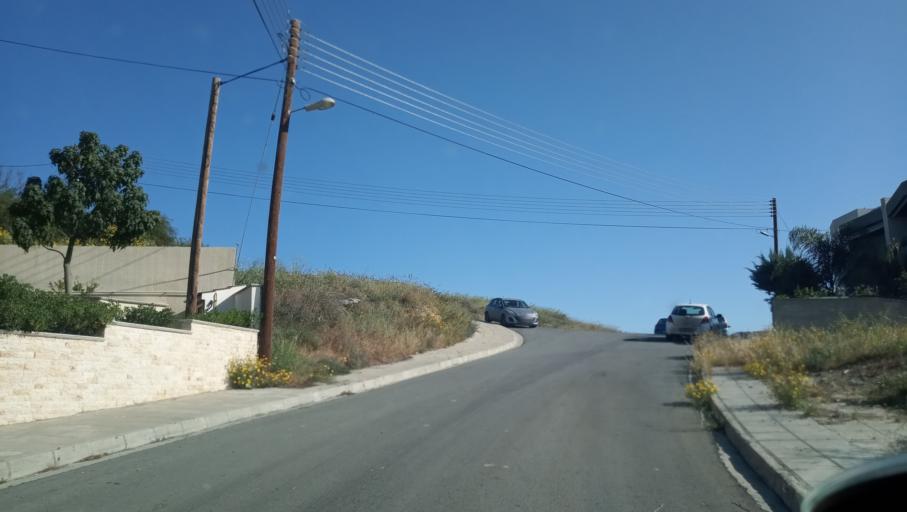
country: CY
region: Lefkosia
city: Tseri
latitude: 35.0709
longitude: 33.3184
